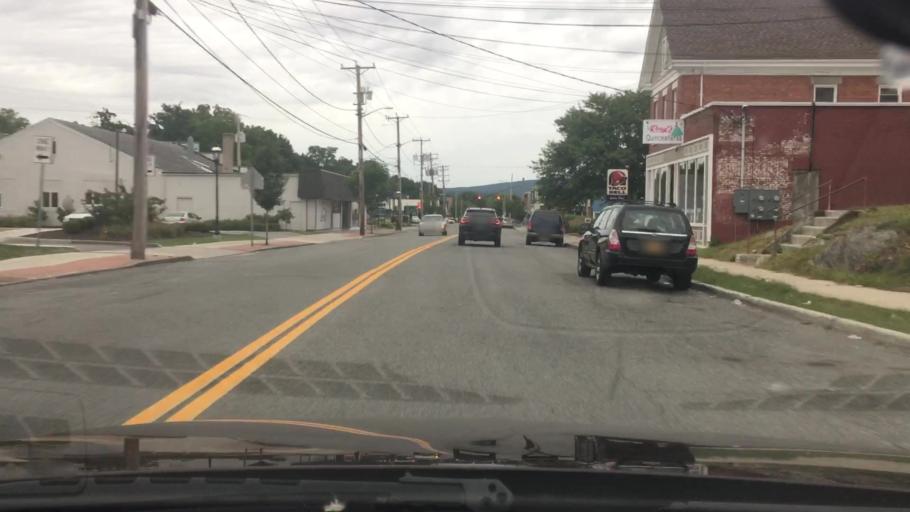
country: US
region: New York
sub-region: Dutchess County
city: Arlington
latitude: 41.6964
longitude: -73.9033
